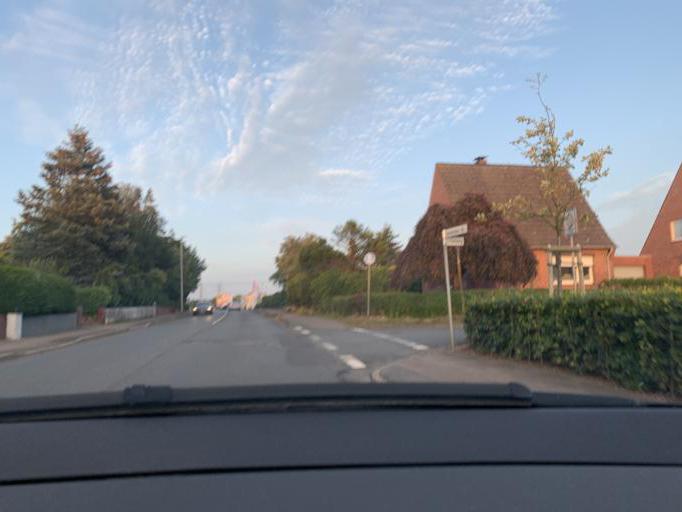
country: DE
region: Schleswig-Holstein
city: Mildstedt
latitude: 54.4711
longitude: 9.0870
